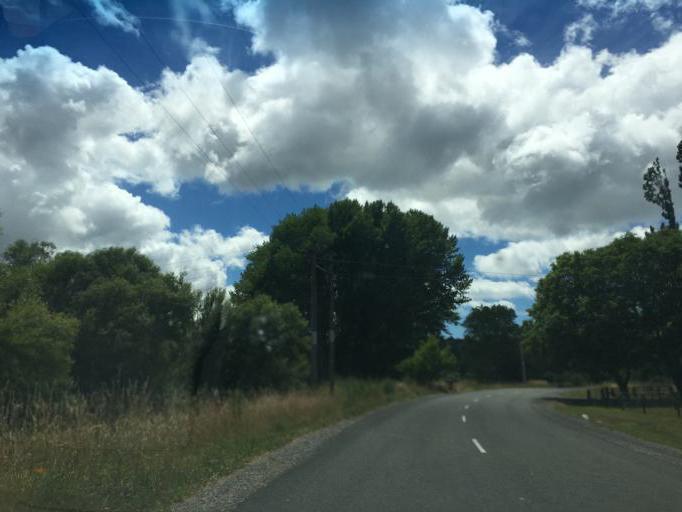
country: NZ
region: Hawke's Bay
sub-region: Hastings District
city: Hastings
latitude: -39.7482
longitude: 176.8810
